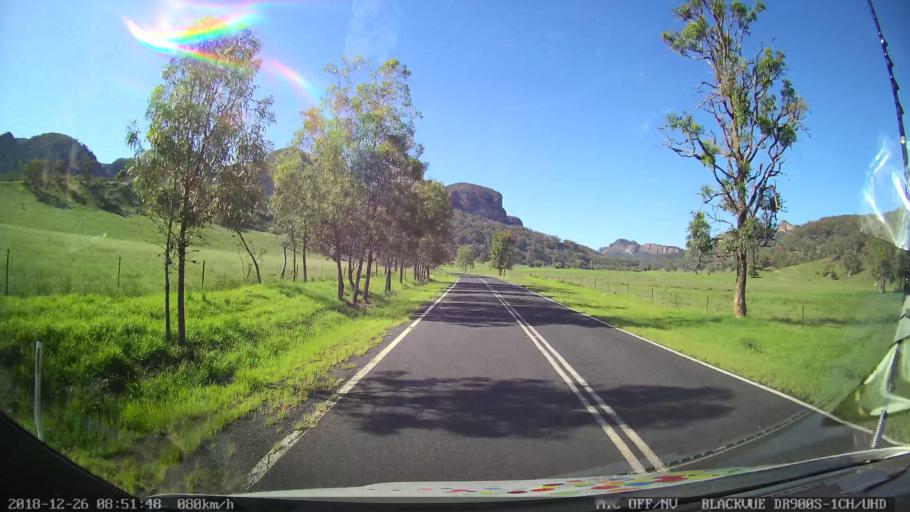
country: AU
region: New South Wales
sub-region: Mid-Western Regional
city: Kandos
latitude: -32.5894
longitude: 150.0881
